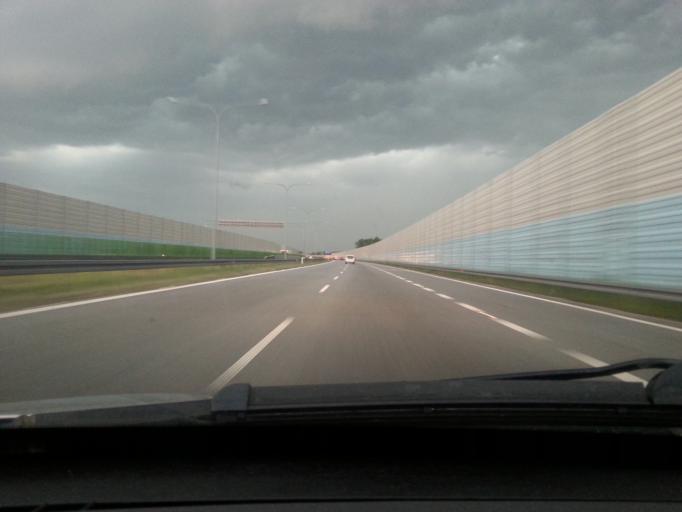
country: PL
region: Lodz Voivodeship
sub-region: powiat Lowicki
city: Lyszkowice
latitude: 51.9869
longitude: 19.8936
